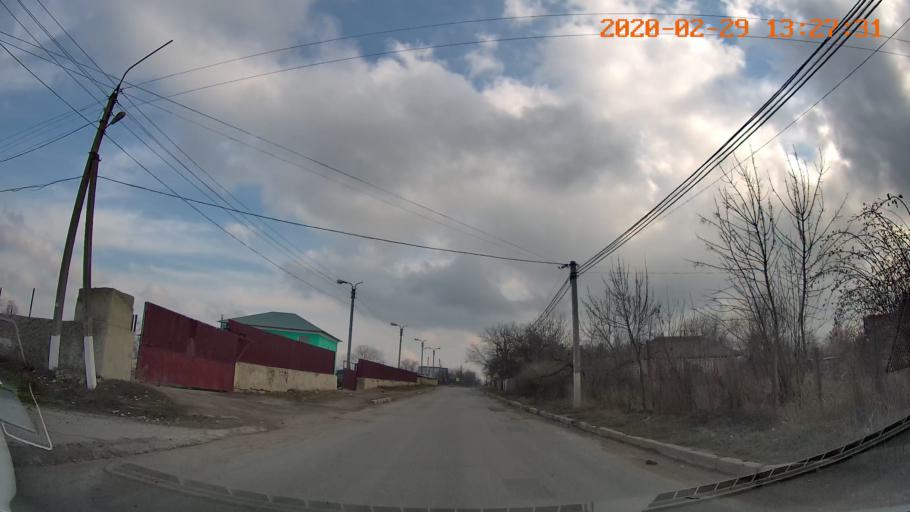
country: MD
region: Telenesti
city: Camenca
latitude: 47.9115
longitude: 28.6422
